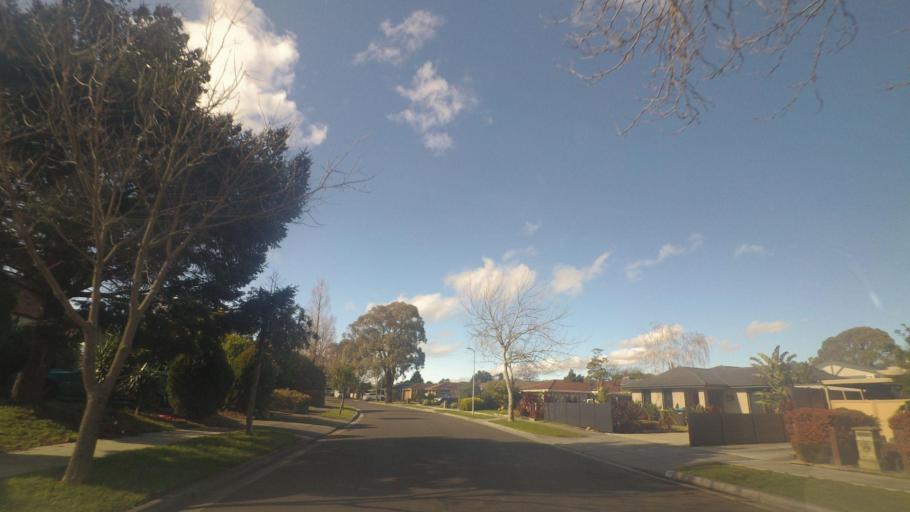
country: AU
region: Victoria
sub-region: Knox
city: Scoresby
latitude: -37.9149
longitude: 145.2530
